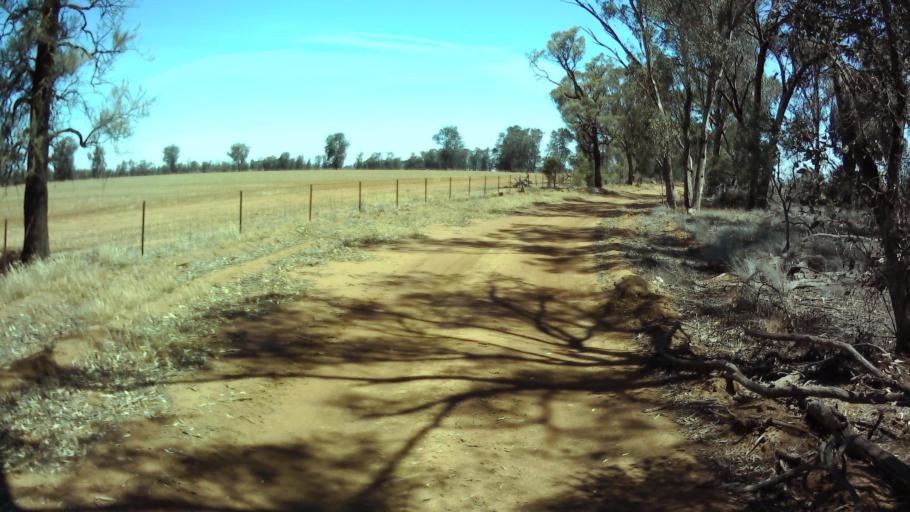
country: AU
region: New South Wales
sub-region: Bland
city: West Wyalong
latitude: -33.9157
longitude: 147.6837
